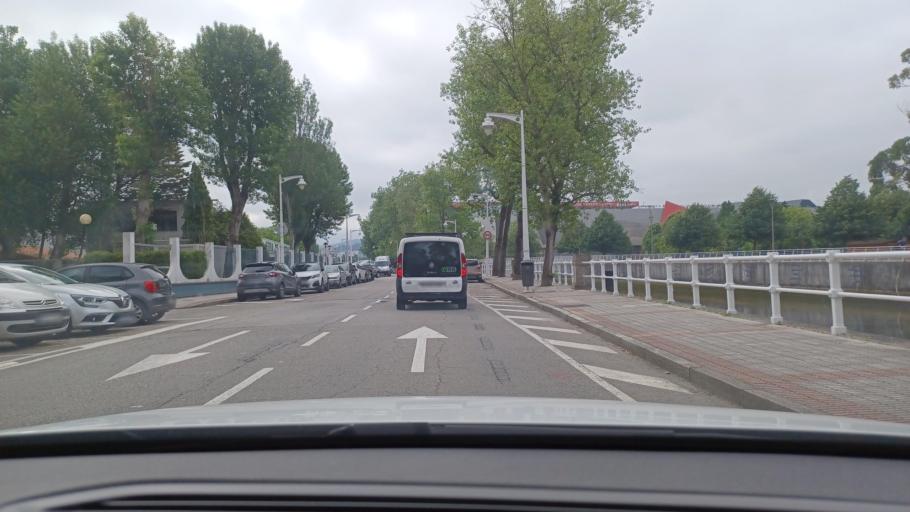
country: ES
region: Asturias
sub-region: Province of Asturias
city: Gijon
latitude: 43.5386
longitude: -5.6402
